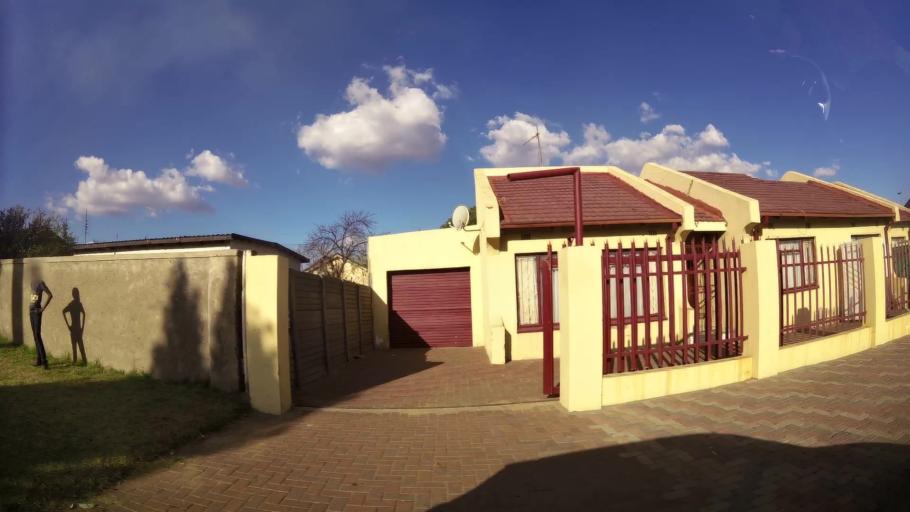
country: ZA
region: Mpumalanga
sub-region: Nkangala District Municipality
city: Witbank
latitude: -25.8710
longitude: 29.1821
